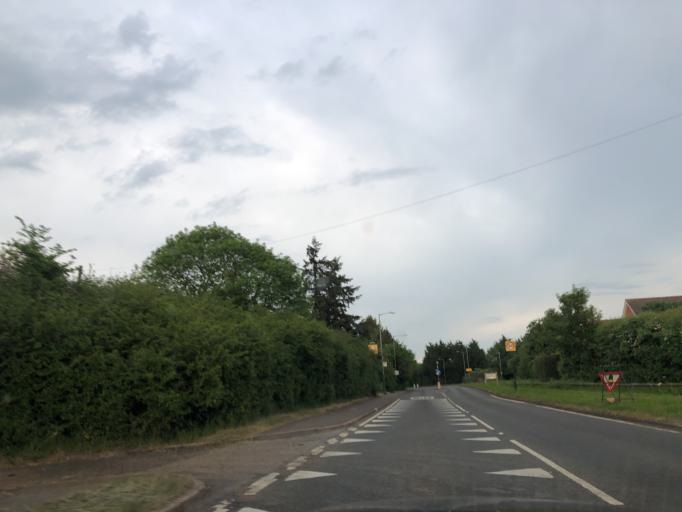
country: GB
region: England
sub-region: Warwickshire
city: Warwick
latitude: 52.2740
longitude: -1.6094
